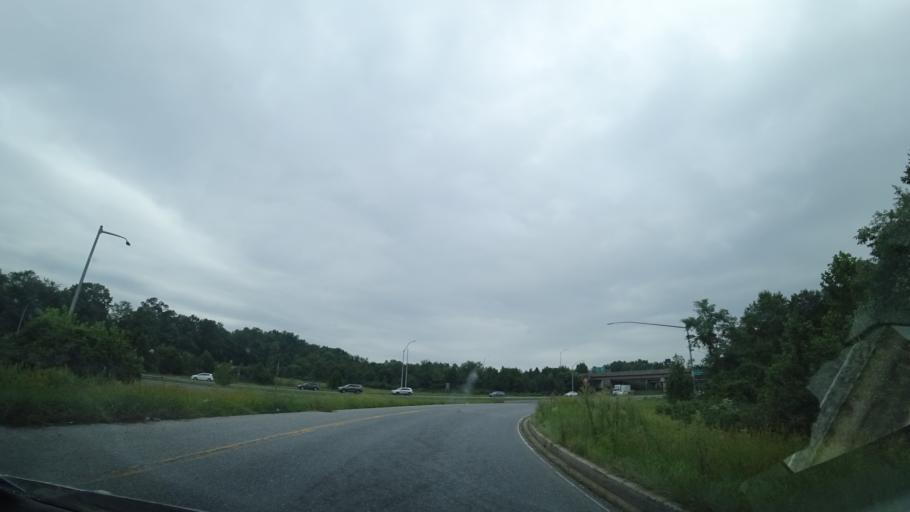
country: US
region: Maryland
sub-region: Howard County
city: Savage
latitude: 39.1368
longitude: -76.8125
